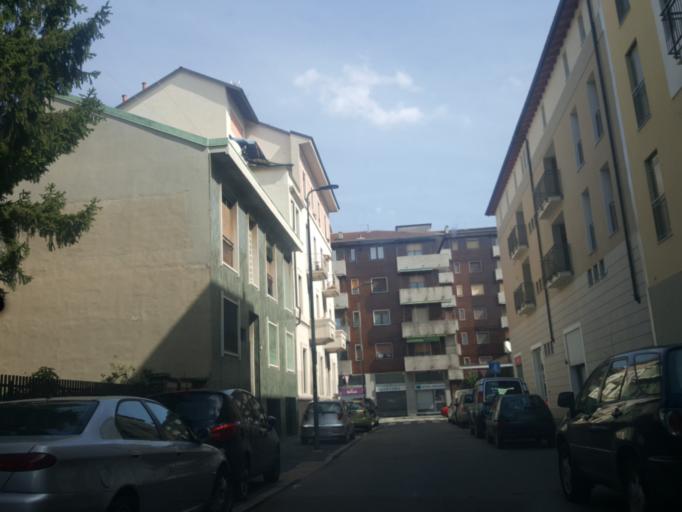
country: IT
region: Lombardy
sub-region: Citta metropolitana di Milano
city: Novate Milanese
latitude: 45.4986
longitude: 9.1432
